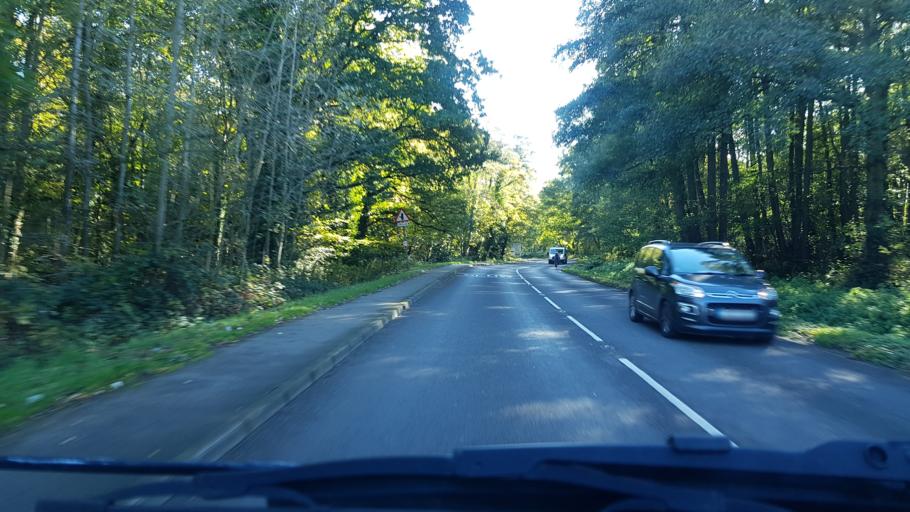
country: GB
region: England
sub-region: Surrey
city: Shalford
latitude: 51.2109
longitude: -0.5520
